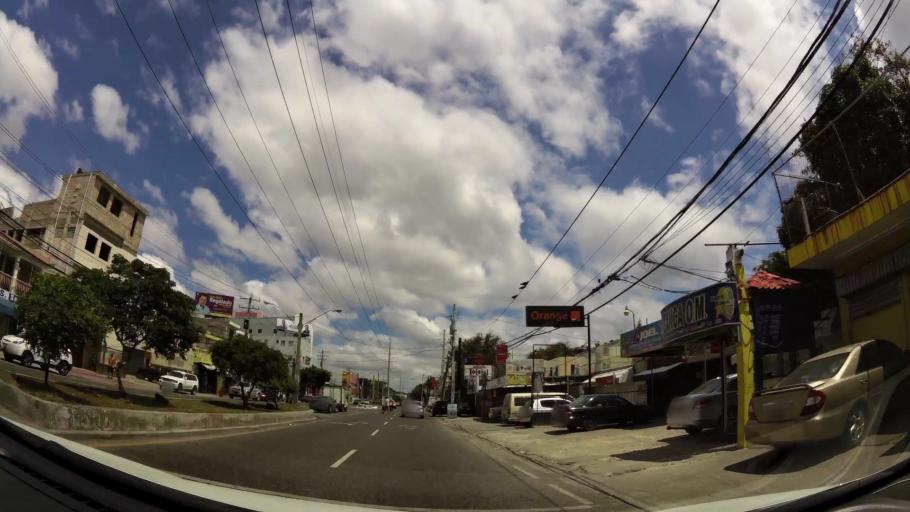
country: DO
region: Nacional
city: Bella Vista
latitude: 18.4347
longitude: -69.9596
